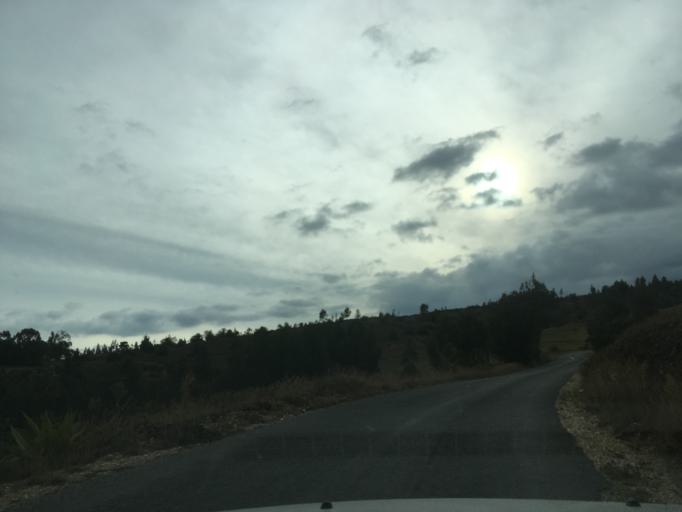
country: CO
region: Boyaca
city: Firavitoba
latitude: 5.6735
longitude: -73.0125
